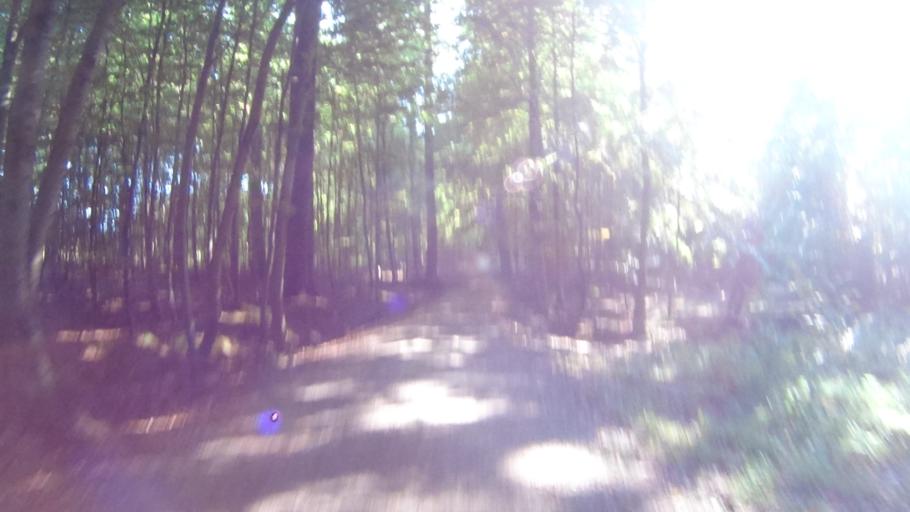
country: BE
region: Flanders
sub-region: Provincie Vlaams-Brabant
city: Wezembeek-Oppem
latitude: 50.8166
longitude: 4.4578
